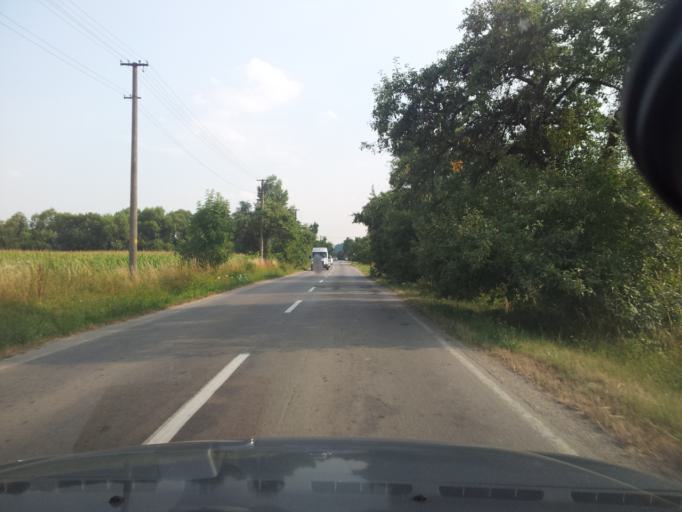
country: SK
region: Nitriansky
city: Banovce nad Bebravou
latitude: 48.7864
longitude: 18.1988
